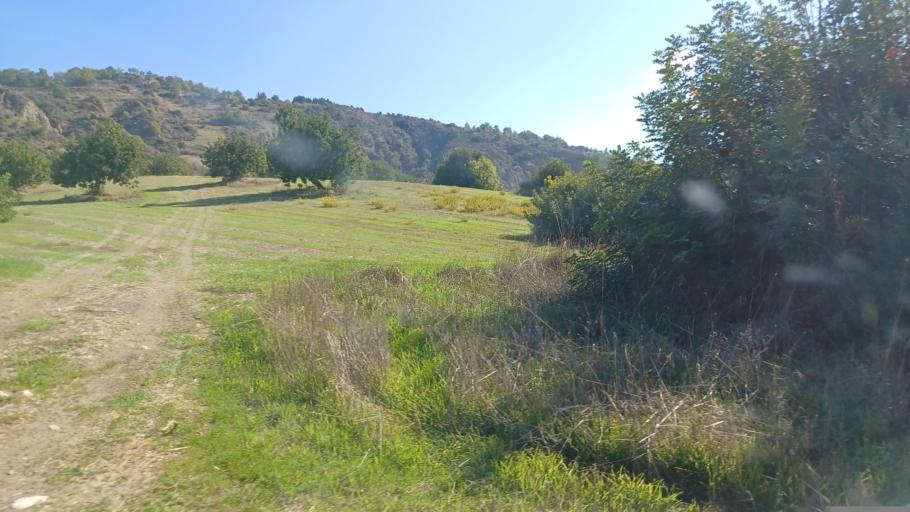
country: CY
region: Pafos
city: Polis
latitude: 35.0333
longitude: 32.4957
